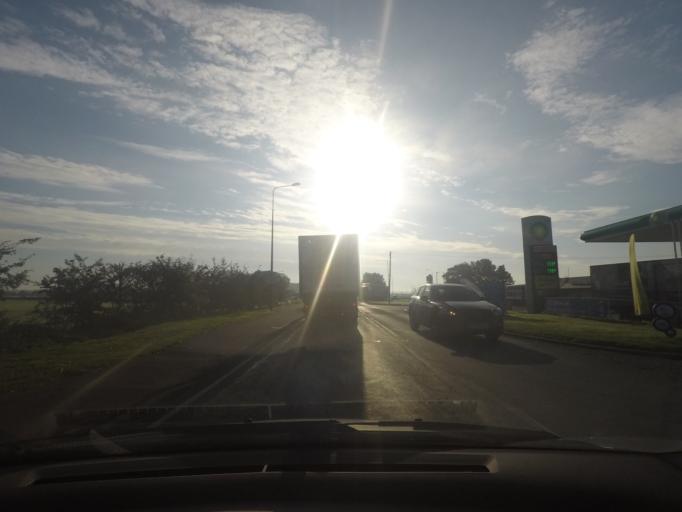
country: GB
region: England
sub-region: East Riding of Yorkshire
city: Londesborough
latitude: 53.8746
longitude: -0.7009
